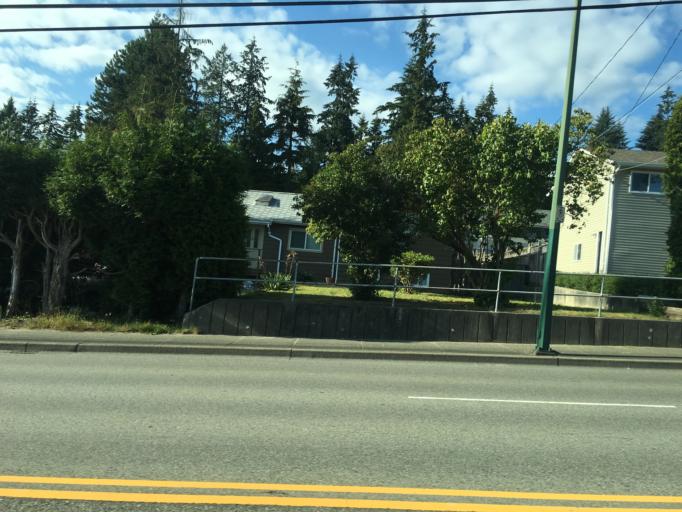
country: CA
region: British Columbia
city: Port Moody
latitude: 49.2490
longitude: -122.8280
